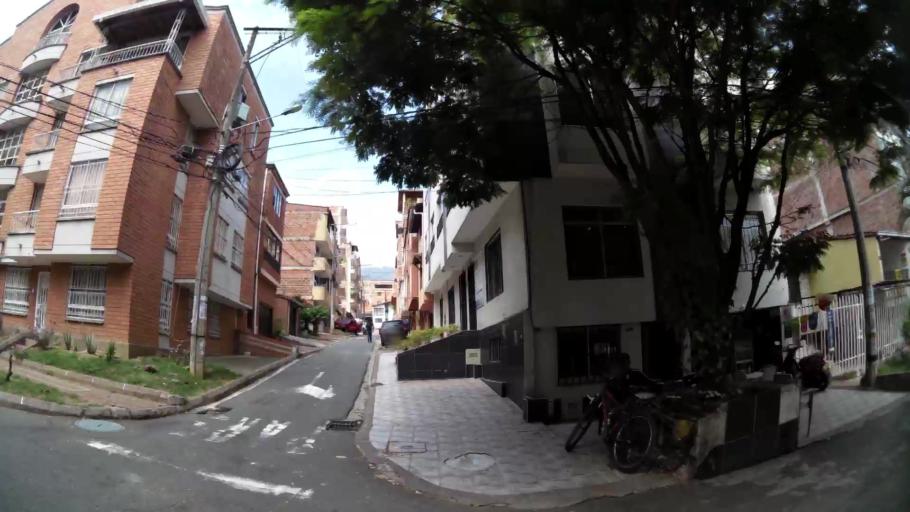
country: CO
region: Antioquia
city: Bello
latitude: 6.3160
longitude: -75.5595
